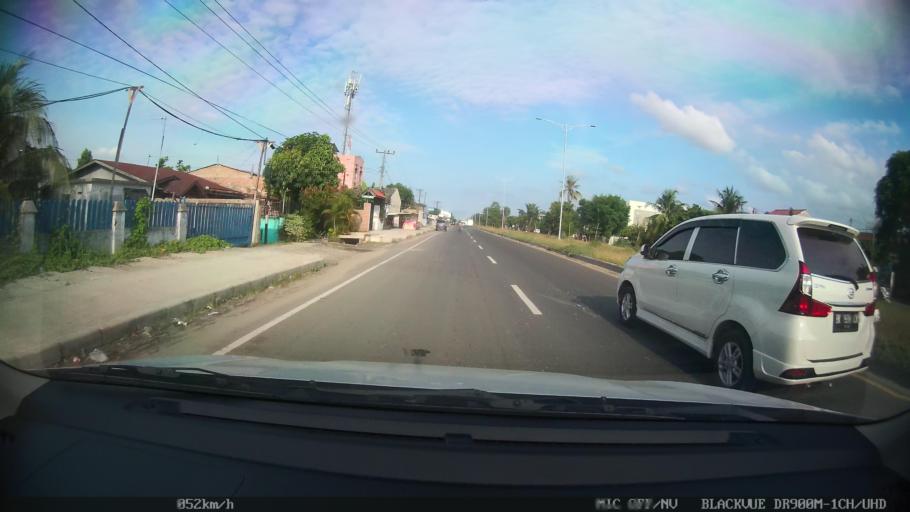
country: ID
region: North Sumatra
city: Sunggal
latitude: 3.6159
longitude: 98.6328
